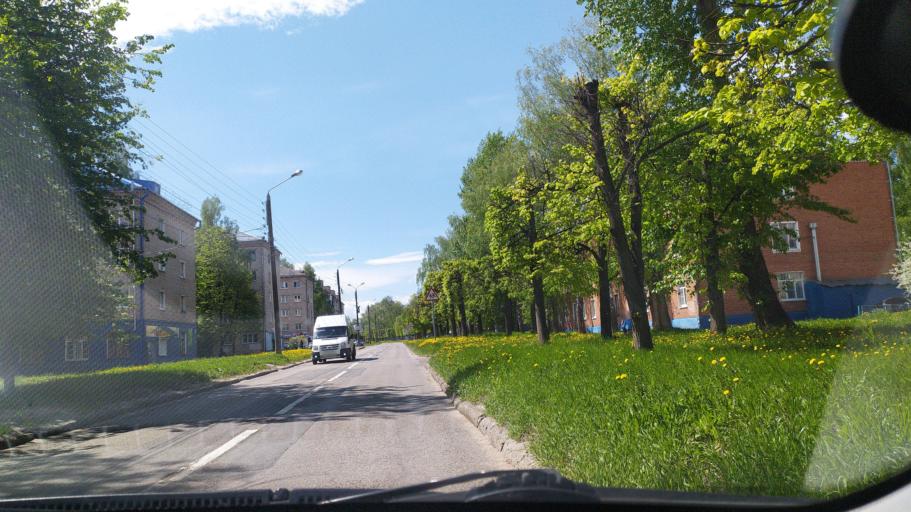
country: RU
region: Chuvashia
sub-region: Cheboksarskiy Rayon
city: Cheboksary
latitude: 56.1422
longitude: 47.2147
